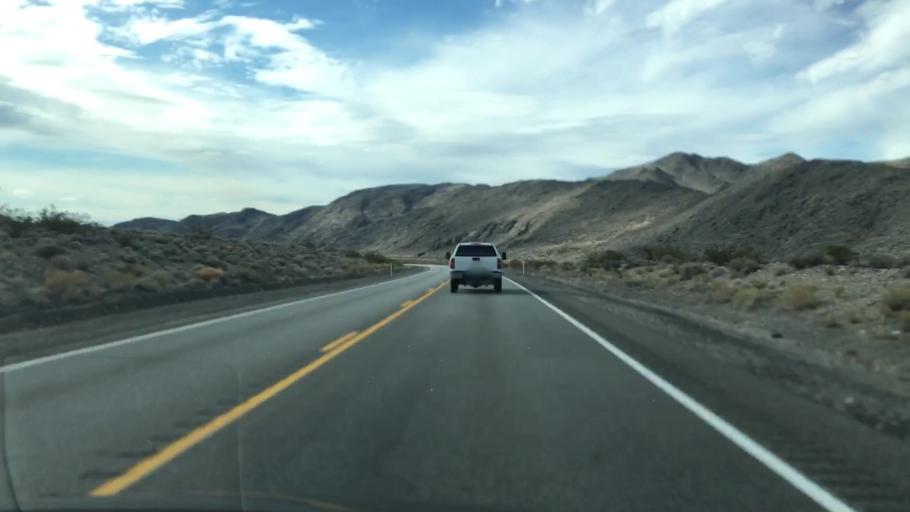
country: US
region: Nevada
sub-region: Nye County
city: Pahrump
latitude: 36.5882
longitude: -116.0512
